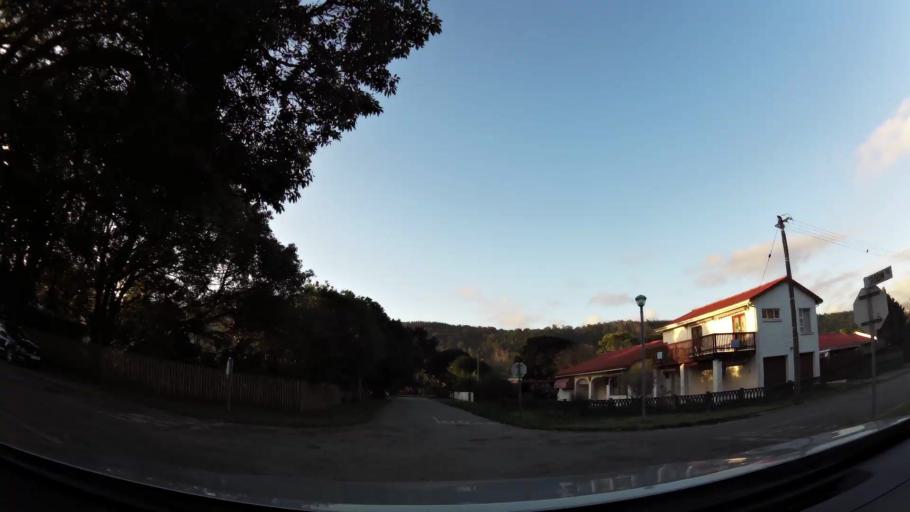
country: ZA
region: Western Cape
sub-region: Eden District Municipality
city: Knysna
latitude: -34.0211
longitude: 22.8077
